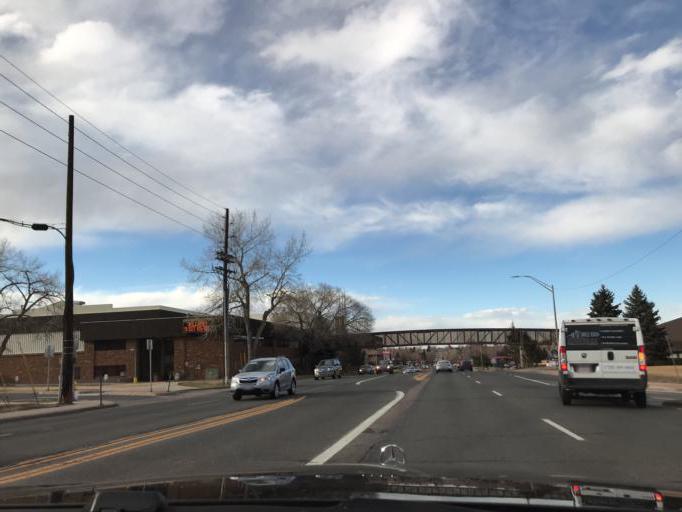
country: US
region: Colorado
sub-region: Jefferson County
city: Arvada
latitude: 39.8085
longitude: -105.1379
